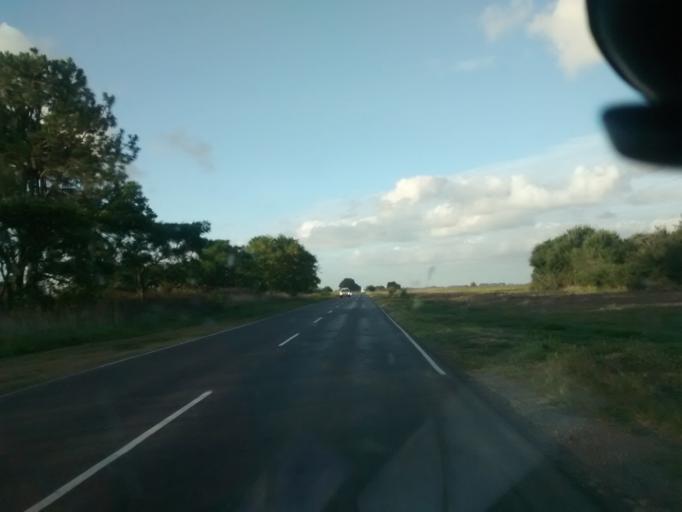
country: AR
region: Buenos Aires
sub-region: Partido de General Belgrano
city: General Belgrano
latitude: -35.8407
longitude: -58.5910
